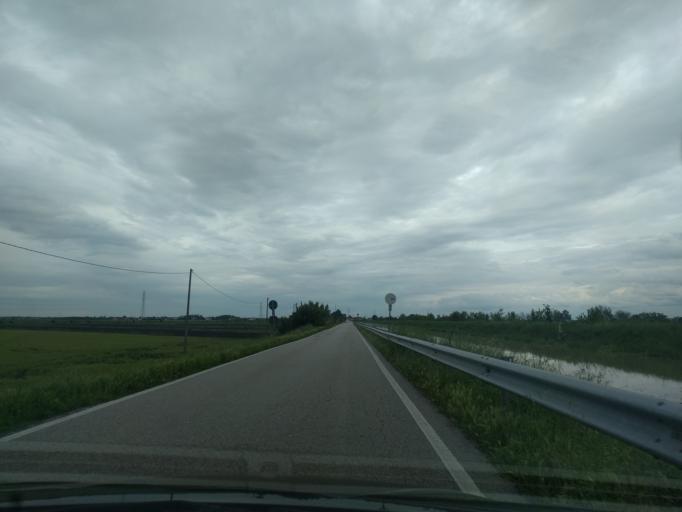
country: IT
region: Veneto
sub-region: Provincia di Rovigo
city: Rovigo
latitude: 45.0887
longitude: 11.8136
